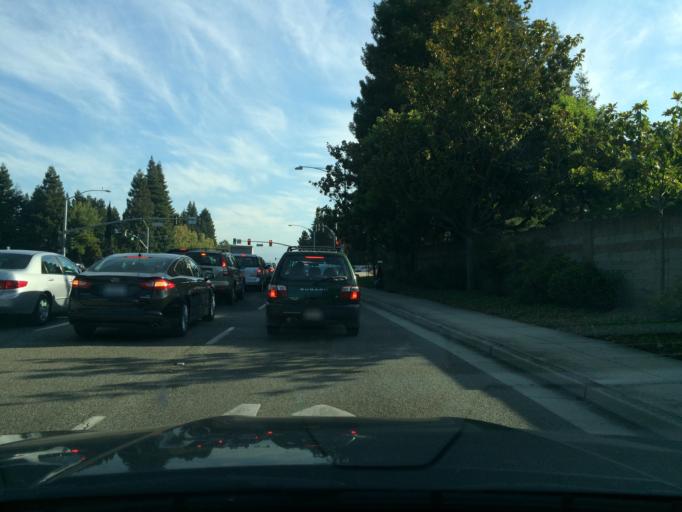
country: US
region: California
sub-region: Santa Clara County
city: Sunnyvale
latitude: 37.3878
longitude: -122.0433
